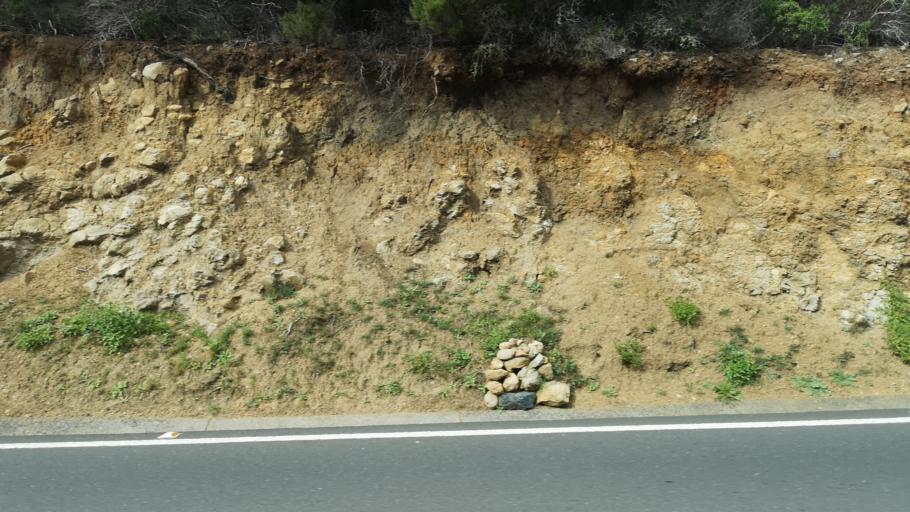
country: ES
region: Canary Islands
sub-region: Provincia de Santa Cruz de Tenerife
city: Alajero
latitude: 28.0987
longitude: -17.1966
